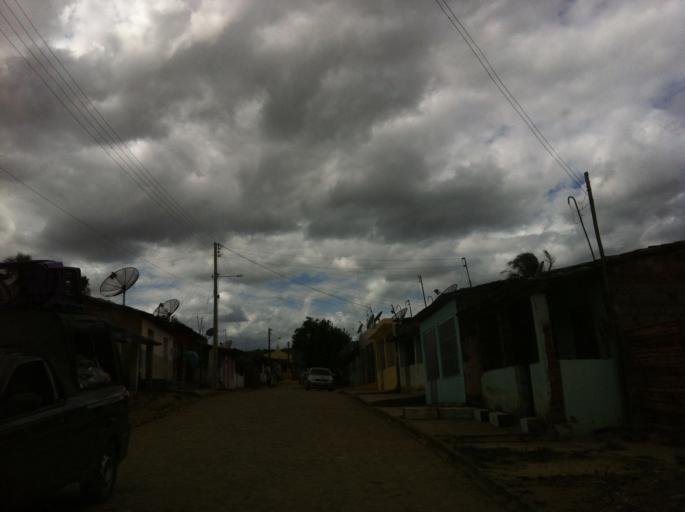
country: BR
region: Alagoas
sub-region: Ibateguara
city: Ibateguara
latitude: -8.9504
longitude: -35.9528
